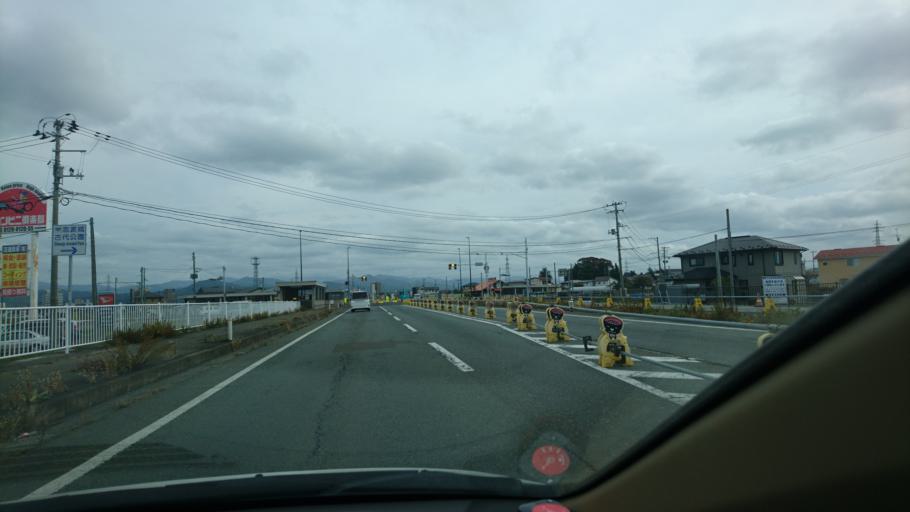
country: JP
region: Iwate
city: Morioka-shi
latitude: 39.6906
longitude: 141.1109
